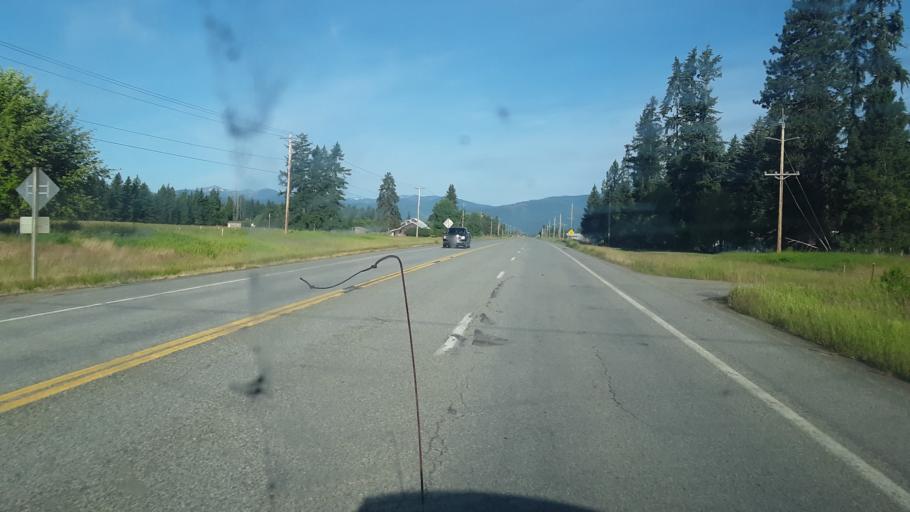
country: US
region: Idaho
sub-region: Boundary County
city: Bonners Ferry
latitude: 48.7316
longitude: -116.2588
